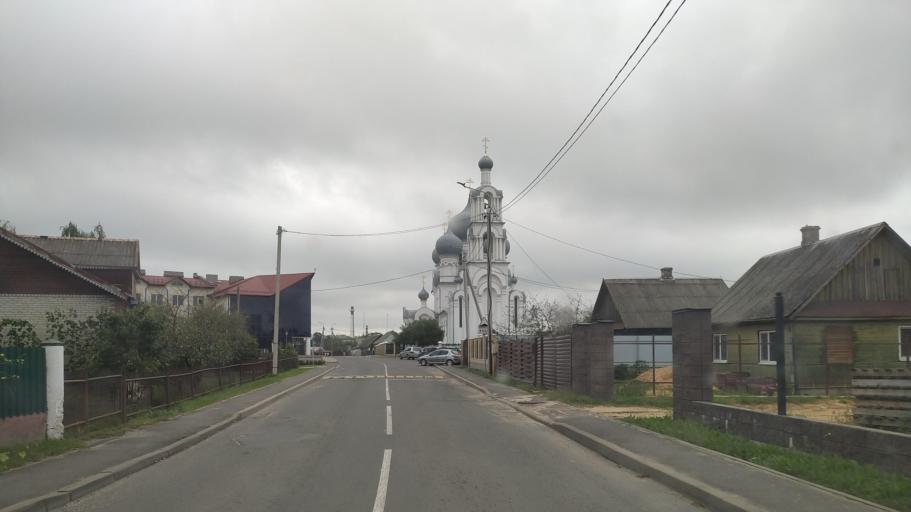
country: BY
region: Brest
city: Byaroza
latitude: 52.5352
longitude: 24.9768
